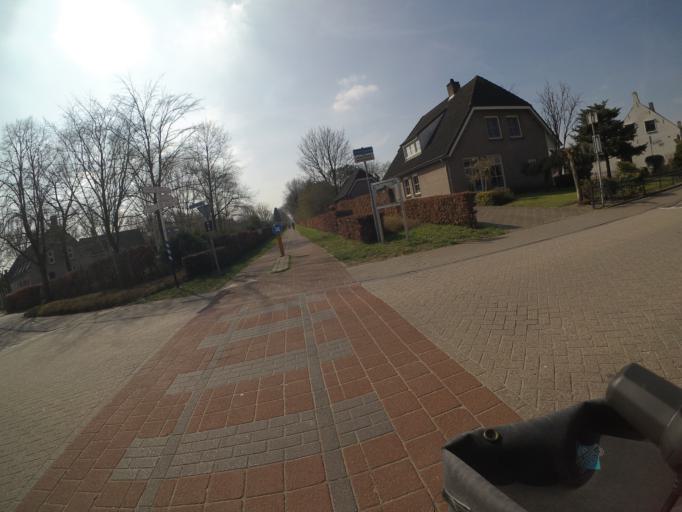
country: NL
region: North Brabant
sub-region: Gemeente Goirle
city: Goirle
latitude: 51.5293
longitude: 5.0223
